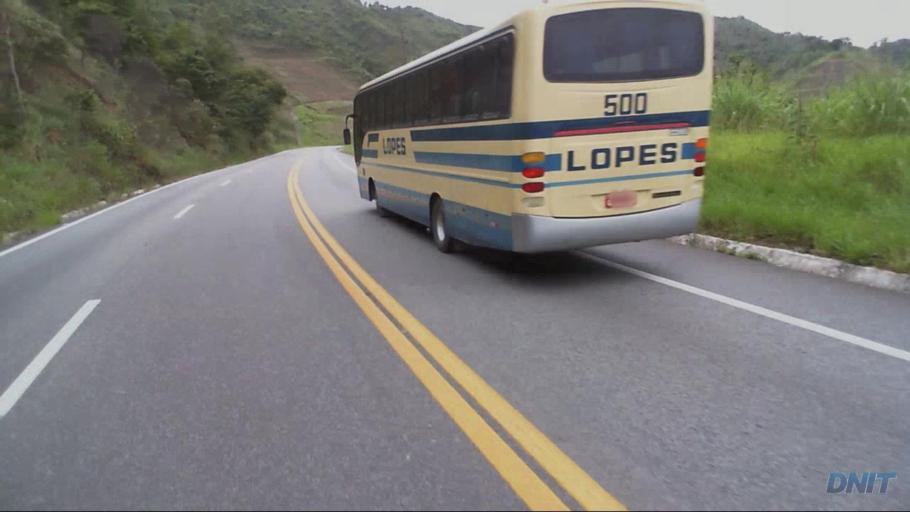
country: BR
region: Minas Gerais
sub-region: Nova Era
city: Nova Era
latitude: -19.6339
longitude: -42.8992
